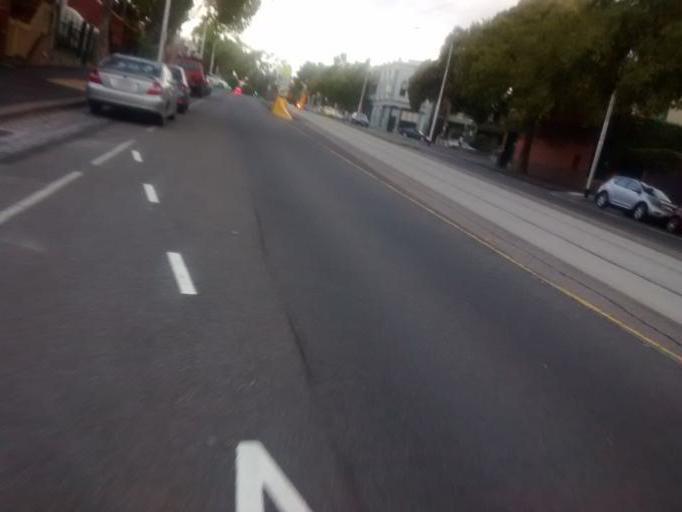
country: AU
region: Victoria
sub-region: Melbourne
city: North Melbourne
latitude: -37.7958
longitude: 144.9466
